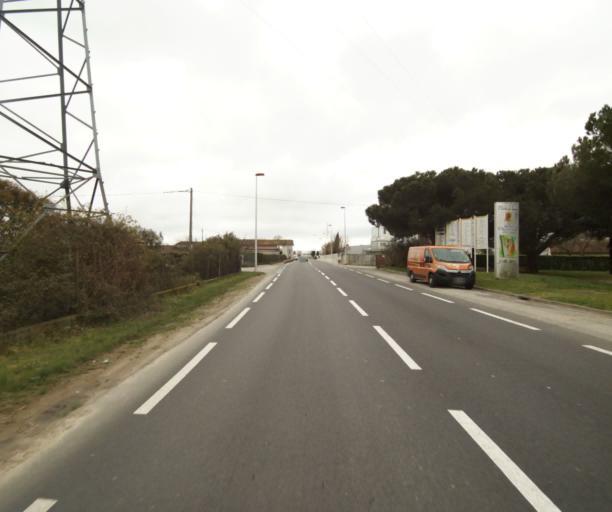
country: FR
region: Midi-Pyrenees
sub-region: Departement de l'Ariege
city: Pamiers
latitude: 43.1315
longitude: 1.6231
